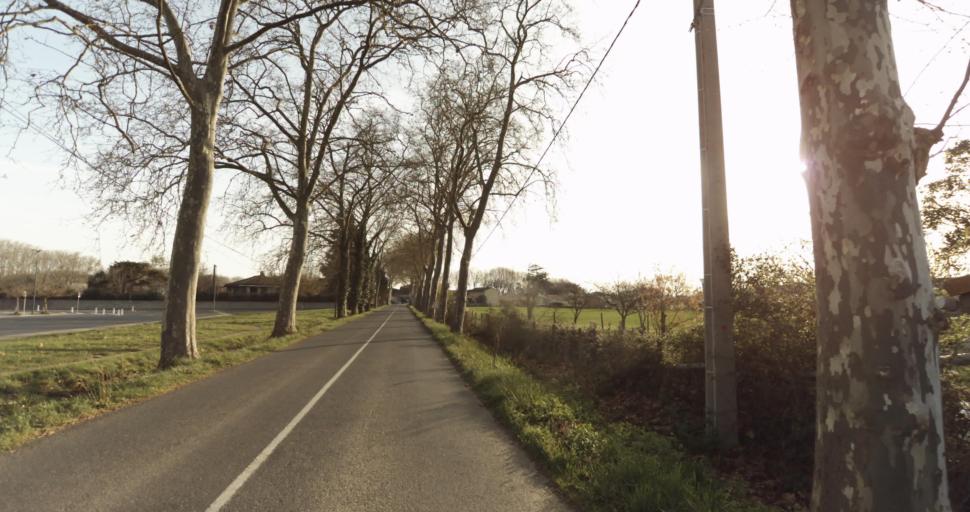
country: FR
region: Midi-Pyrenees
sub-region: Departement du Tarn
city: Saint-Sulpice-la-Pointe
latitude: 43.7760
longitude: 1.6691
